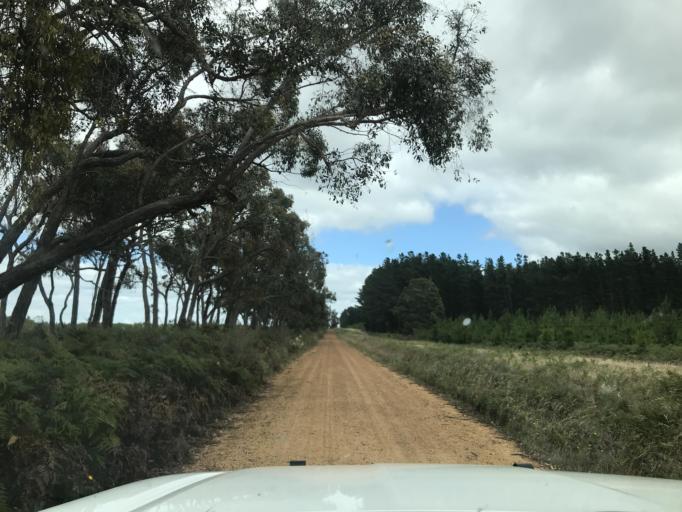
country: AU
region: South Australia
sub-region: Wattle Range
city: Penola
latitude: -37.3172
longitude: 141.1571
